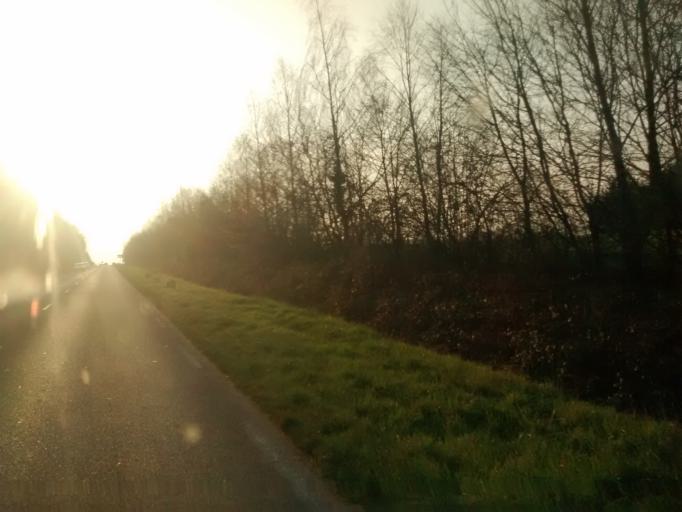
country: FR
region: Brittany
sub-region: Departement d'Ille-et-Vilaine
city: Chavagne
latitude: 48.0600
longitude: -1.7835
